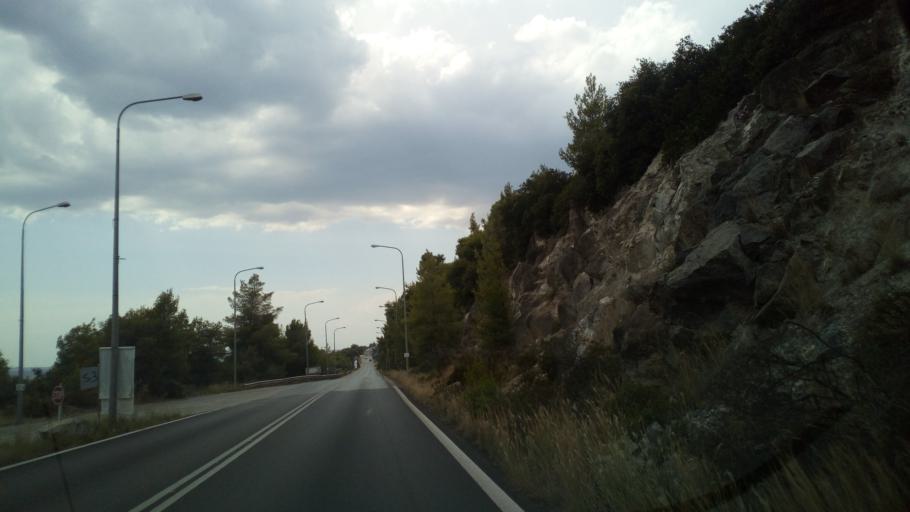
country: GR
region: Central Macedonia
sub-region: Nomos Chalkidikis
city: Ormylia
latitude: 40.2609
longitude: 23.4860
